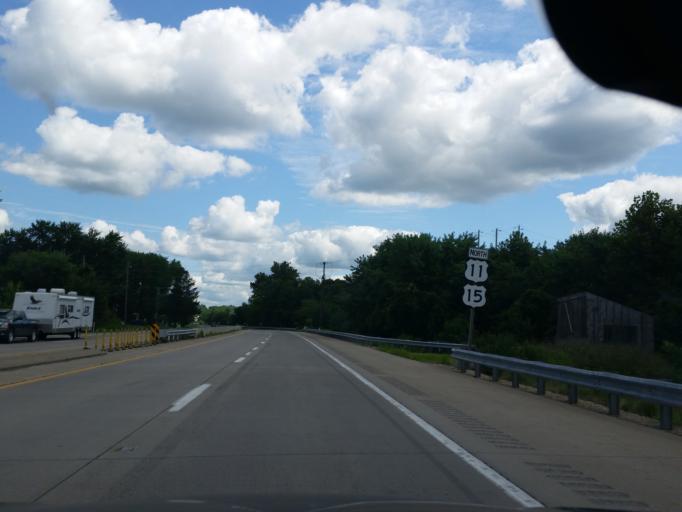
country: US
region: Pennsylvania
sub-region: Dauphin County
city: Millersburg
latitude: 40.6554
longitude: -76.9218
